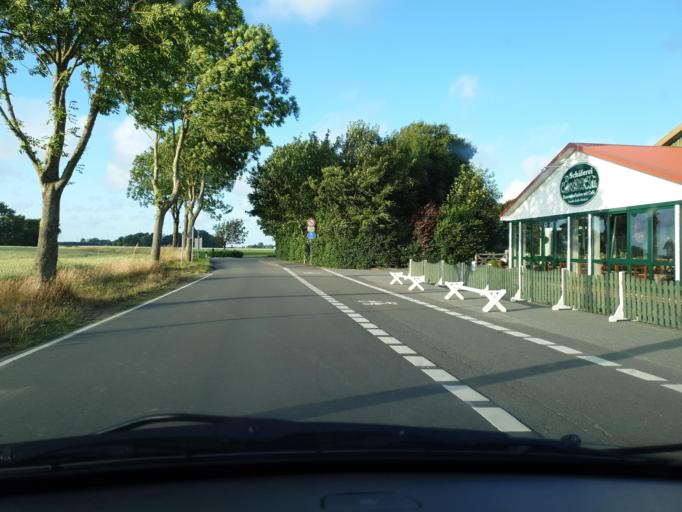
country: DE
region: Schleswig-Holstein
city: Busumer Deichhausen
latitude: 54.1398
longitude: 8.8959
